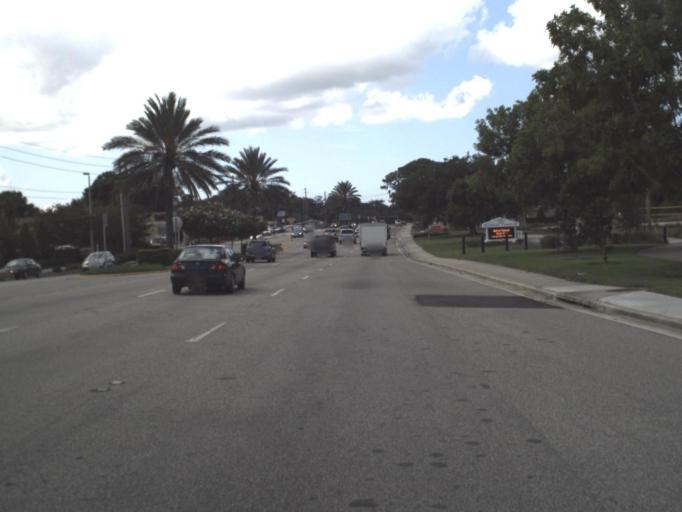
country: US
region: Florida
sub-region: Pinellas County
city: Largo
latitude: 27.9146
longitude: -82.7879
